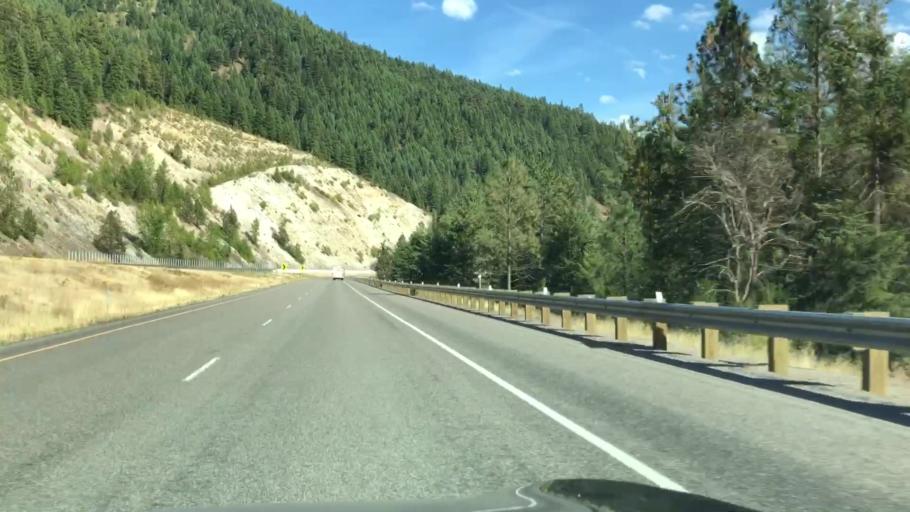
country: US
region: Montana
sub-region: Sanders County
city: Thompson Falls
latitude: 47.3124
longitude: -115.2147
